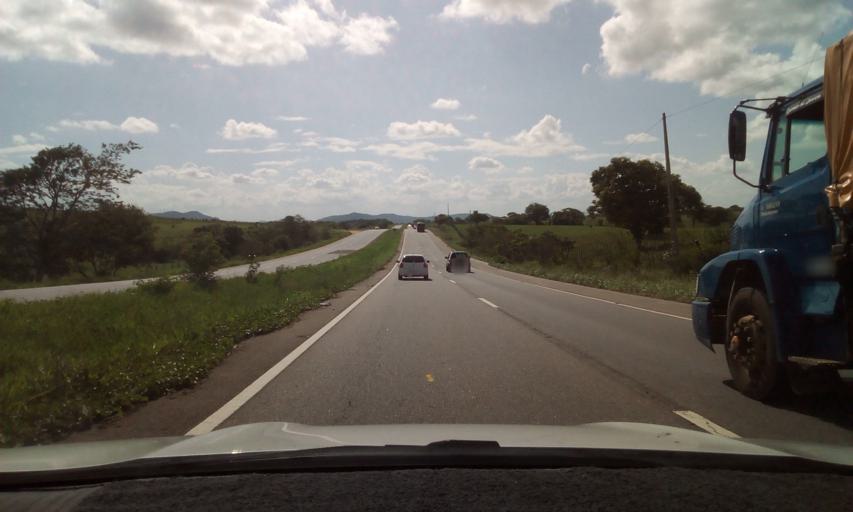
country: BR
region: Paraiba
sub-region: Pilar
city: Pilar
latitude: -7.1810
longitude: -35.3117
